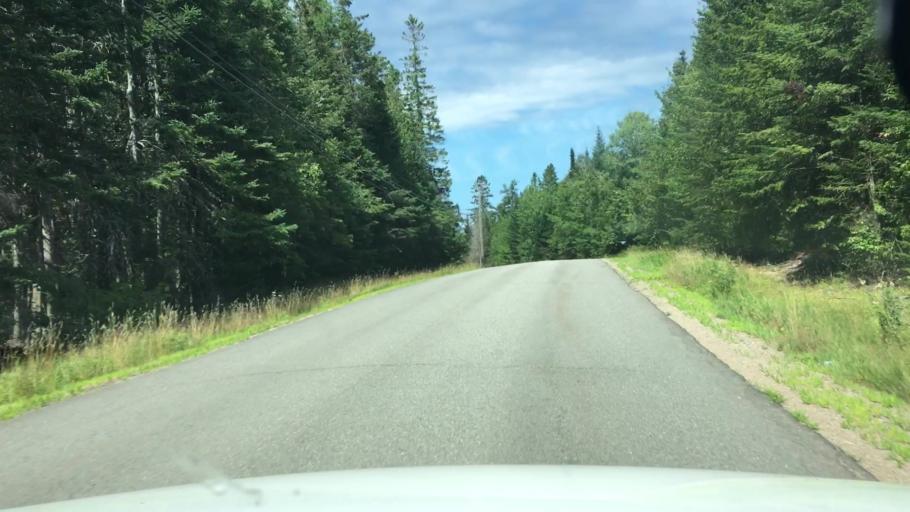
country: CA
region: New Brunswick
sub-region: Charlotte County
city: Saint Andrews
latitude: 44.9803
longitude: -67.0683
